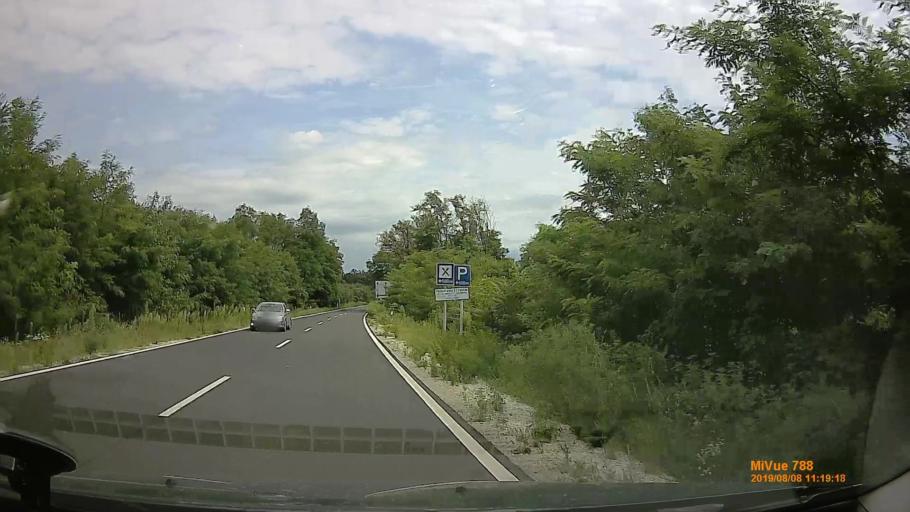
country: HU
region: Somogy
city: Balatonbereny
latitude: 46.6752
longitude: 17.3336
